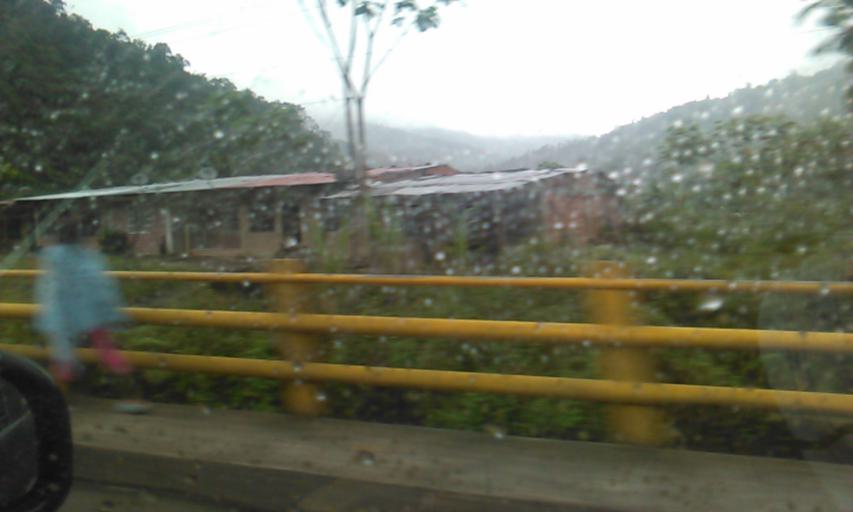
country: CO
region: Valle del Cauca
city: Buenaventura
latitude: 3.8656
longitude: -76.8289
